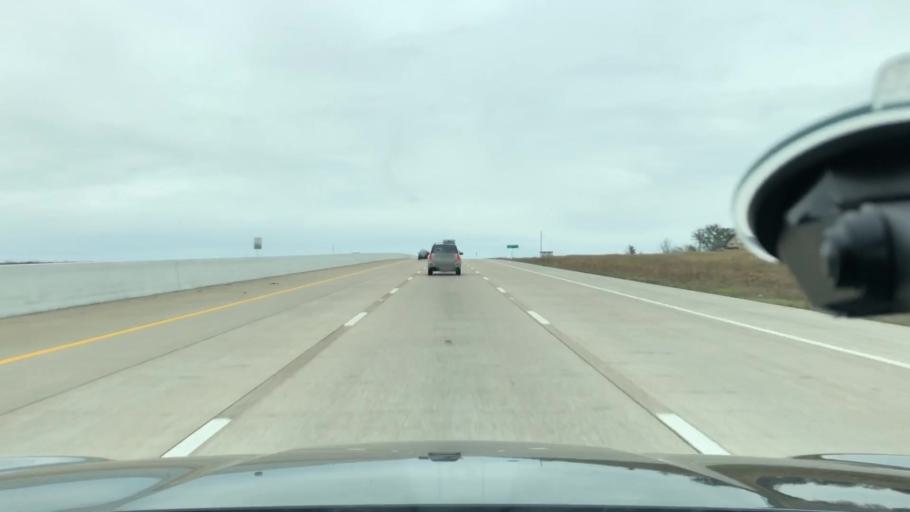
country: US
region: Texas
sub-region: Ellis County
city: Plum Grove
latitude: 32.1411
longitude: -96.9433
